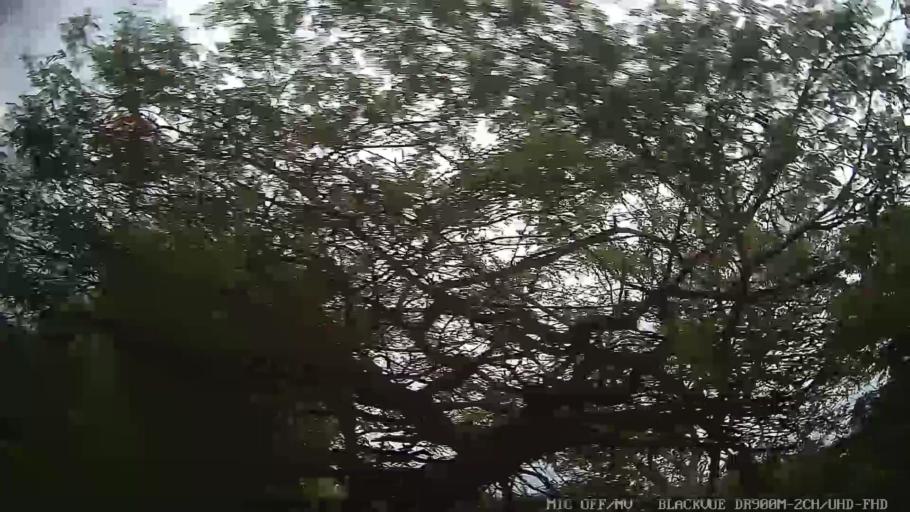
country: BR
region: Sao Paulo
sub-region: Amparo
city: Amparo
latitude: -22.6967
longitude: -46.7621
